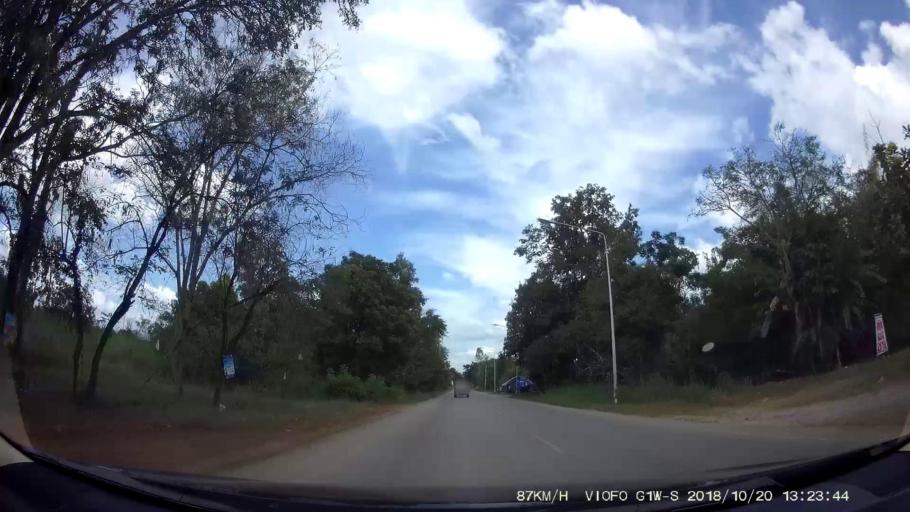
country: TH
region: Chaiyaphum
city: Khon San
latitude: 16.5870
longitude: 101.9232
